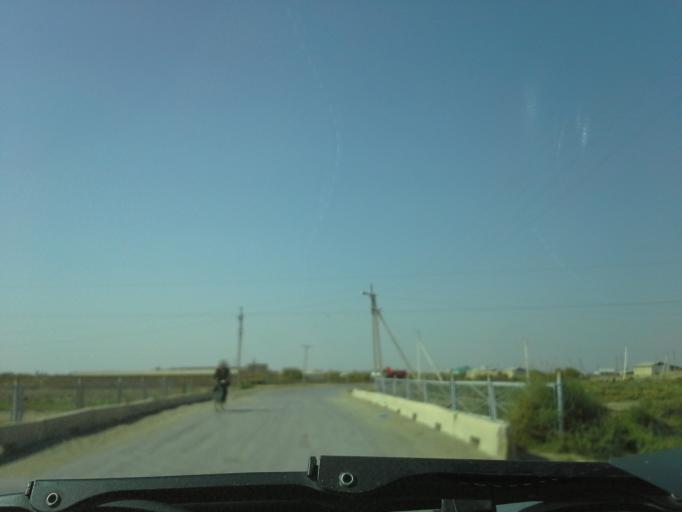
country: TM
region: Lebap
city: Atamyrat
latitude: 37.8217
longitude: 65.1863
